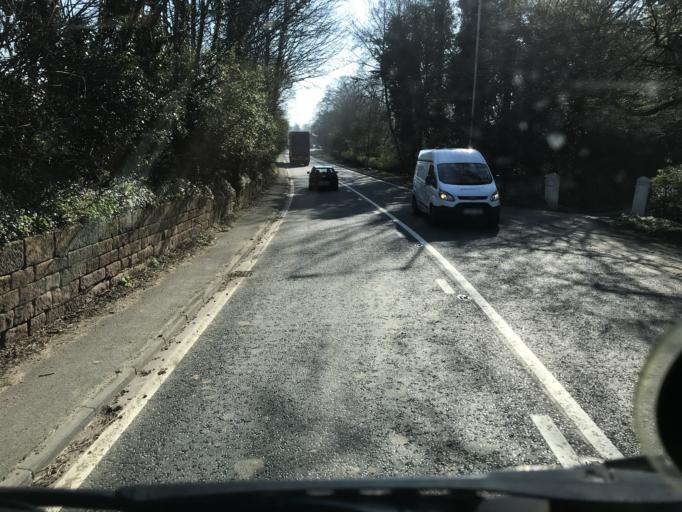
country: GB
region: England
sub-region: Cheshire West and Chester
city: Guilden Sutton
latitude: 53.1796
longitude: -2.8361
